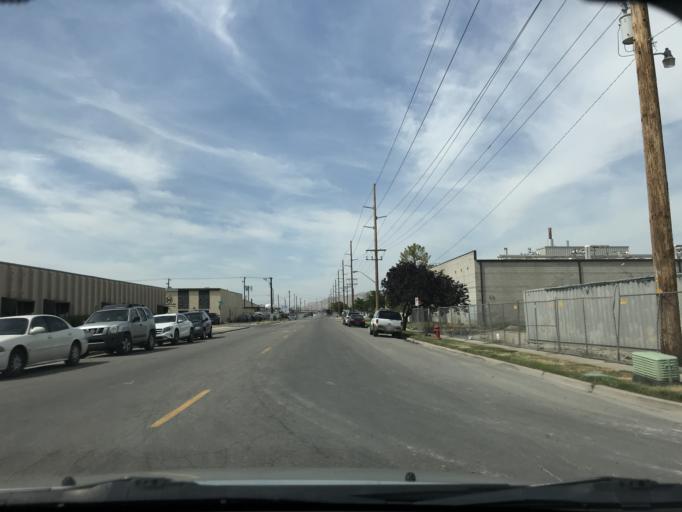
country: US
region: Utah
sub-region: Salt Lake County
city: Centerfield
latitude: 40.6935
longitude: -111.9055
